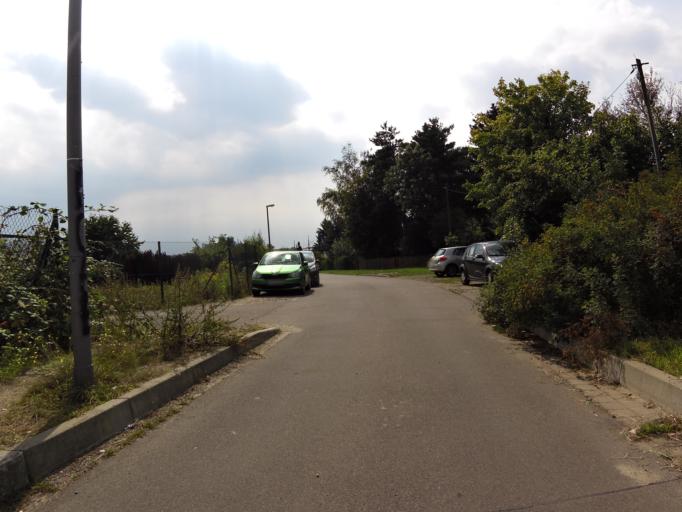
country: DE
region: Saxony
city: Leipzig
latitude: 51.3774
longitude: 12.3303
